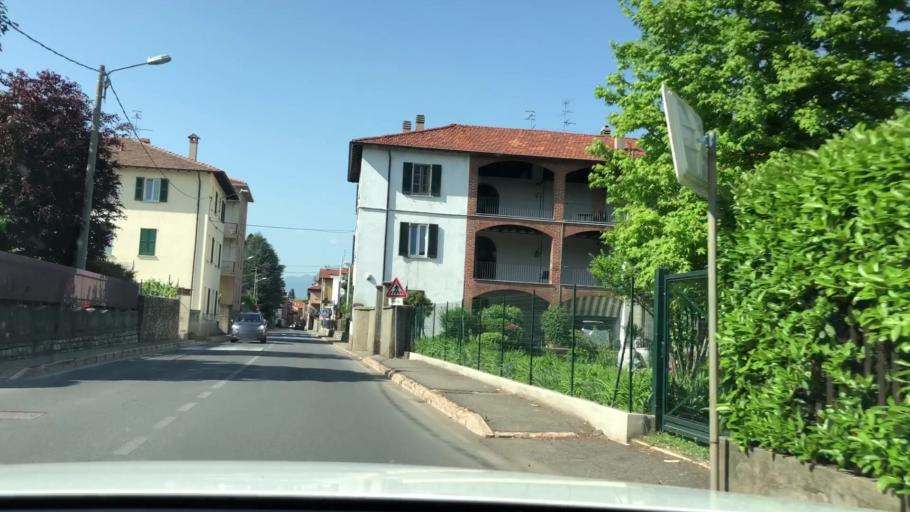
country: IT
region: Lombardy
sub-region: Provincia di Como
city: Cadorago-Caslino al Piano
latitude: 45.7223
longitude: 9.0387
